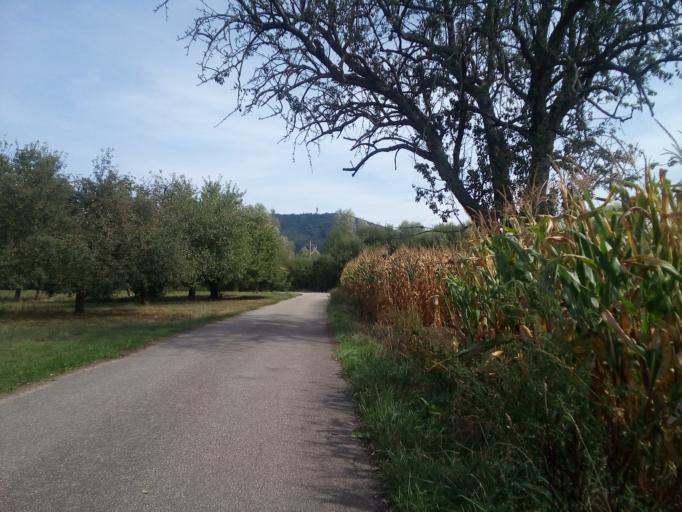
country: DE
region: Baden-Wuerttemberg
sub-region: Karlsruhe Region
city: Sinzheim
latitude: 48.7534
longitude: 8.1518
